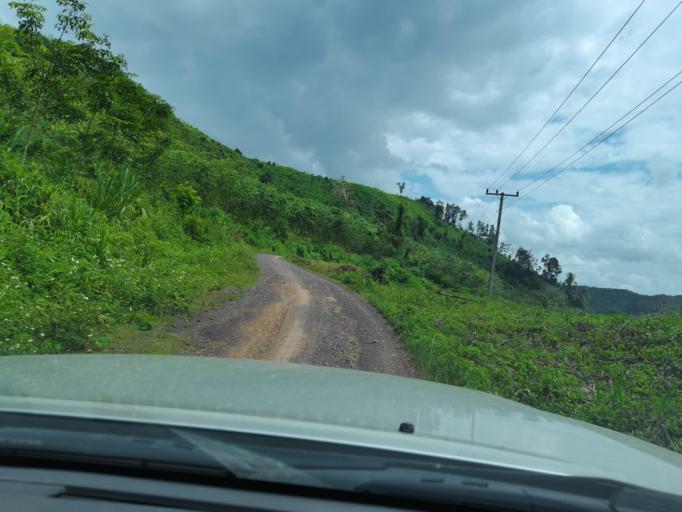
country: LA
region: Loungnamtha
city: Muang Long
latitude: 20.7152
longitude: 101.0140
